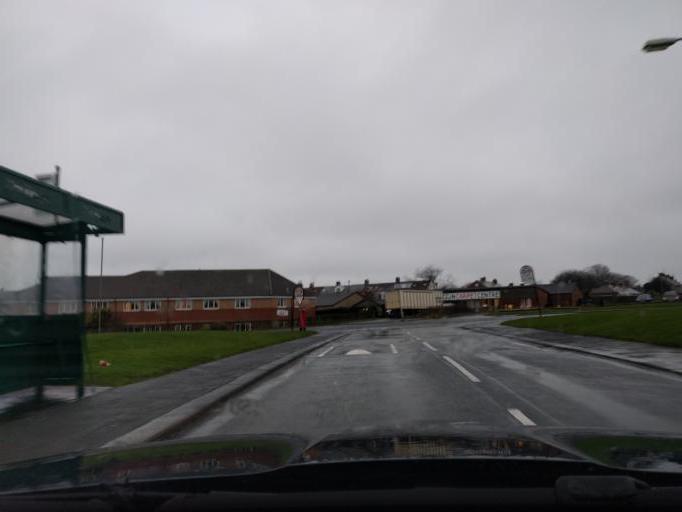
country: GB
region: England
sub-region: Northumberland
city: Newbiggin-by-the-Sea
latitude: 55.1864
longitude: -1.5149
